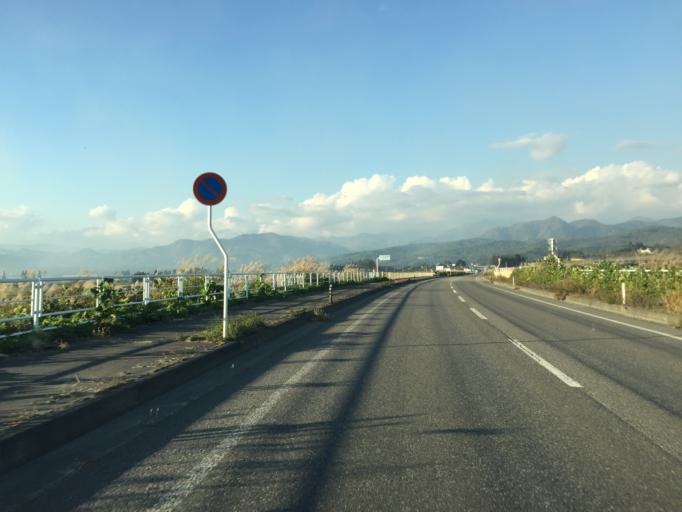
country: JP
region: Fukushima
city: Kitakata
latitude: 37.6762
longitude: 139.8878
